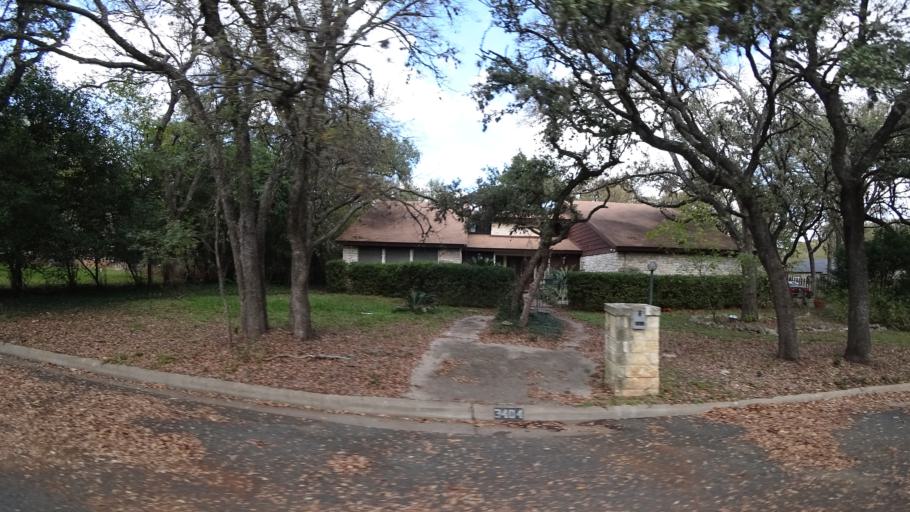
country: US
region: Texas
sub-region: Travis County
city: Shady Hollow
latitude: 30.1711
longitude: -97.8555
